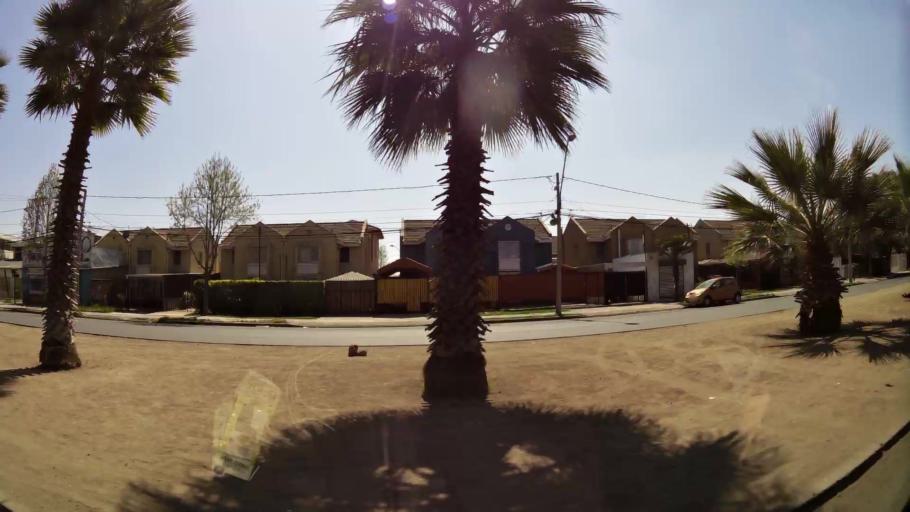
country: CL
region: Santiago Metropolitan
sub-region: Provincia de Santiago
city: Lo Prado
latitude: -33.3578
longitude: -70.7360
